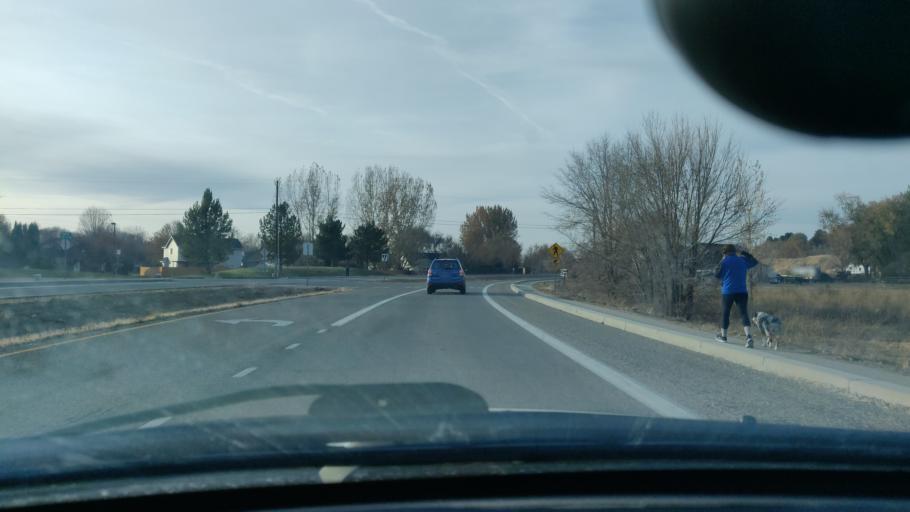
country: US
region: Idaho
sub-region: Ada County
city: Eagle
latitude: 43.6868
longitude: -116.3004
